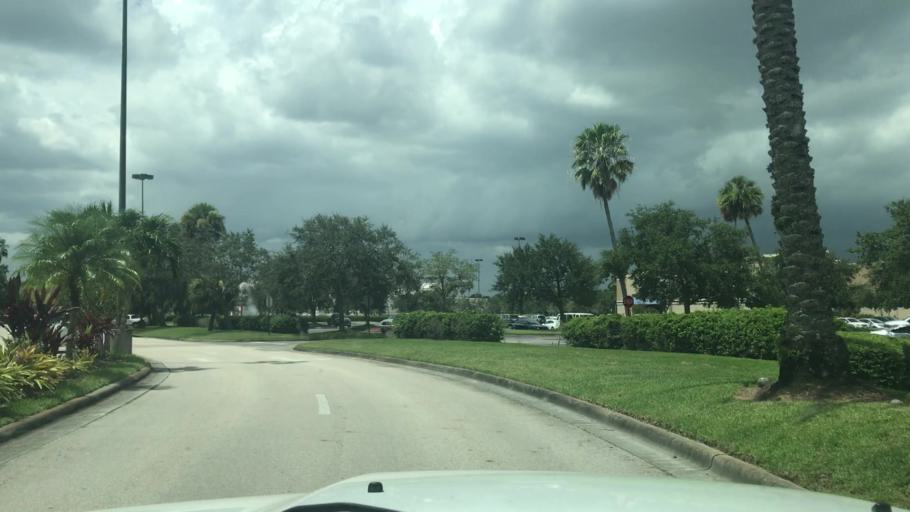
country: US
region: Florida
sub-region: Indian River County
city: West Vero Corridor
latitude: 27.6399
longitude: -80.4543
